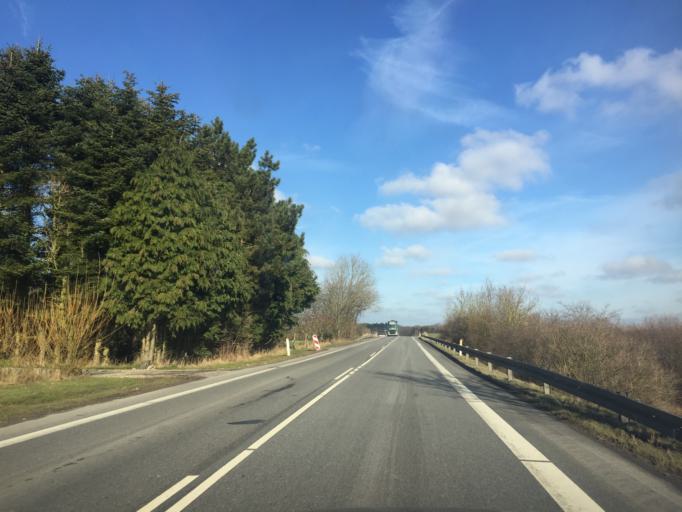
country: DK
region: South Denmark
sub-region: Assens Kommune
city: Vissenbjerg
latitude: 55.4237
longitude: 10.1797
